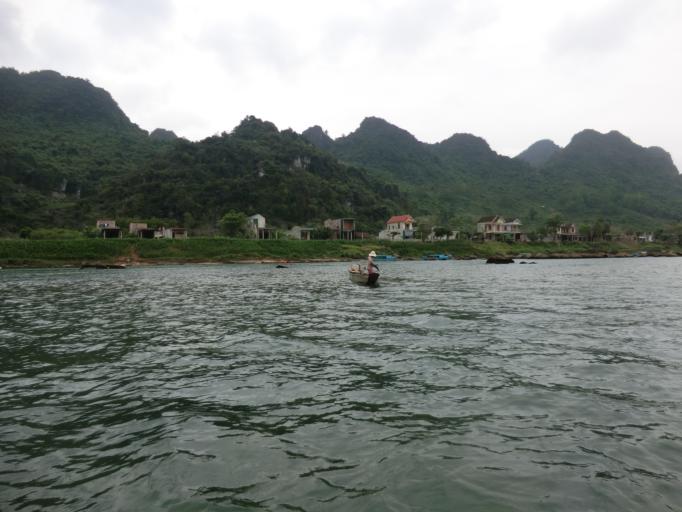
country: VN
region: Quang Binh
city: Ba Don
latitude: 17.5976
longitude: 106.2874
